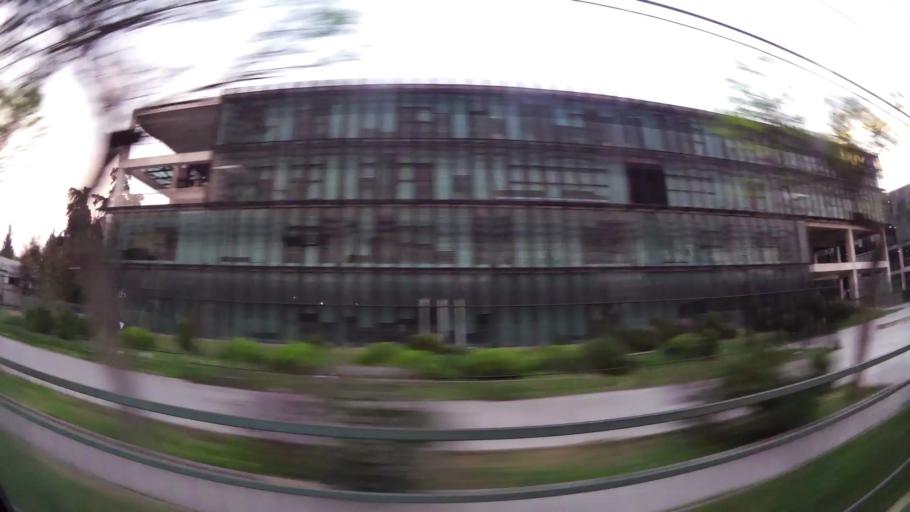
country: CL
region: Santiago Metropolitan
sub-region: Provincia de Santiago
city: Lo Prado
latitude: -33.5109
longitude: -70.7520
